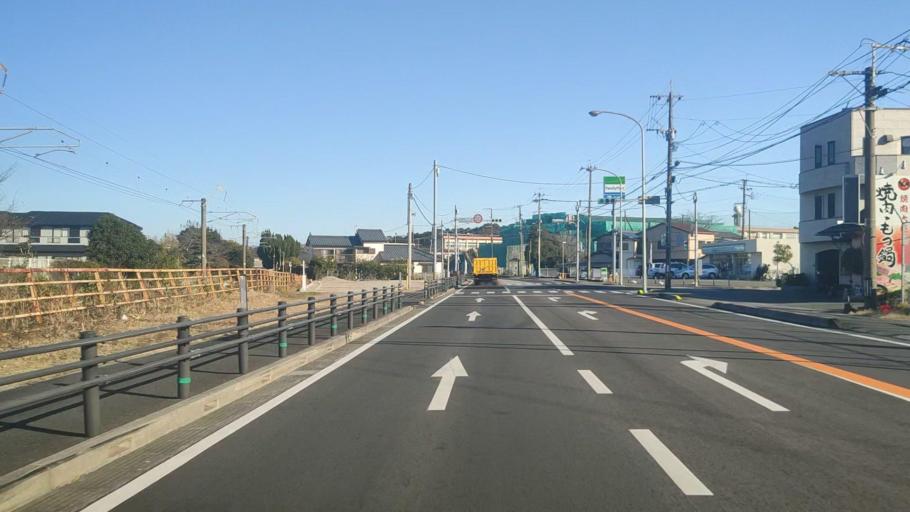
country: JP
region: Miyazaki
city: Nobeoka
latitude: 32.5193
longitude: 131.6829
